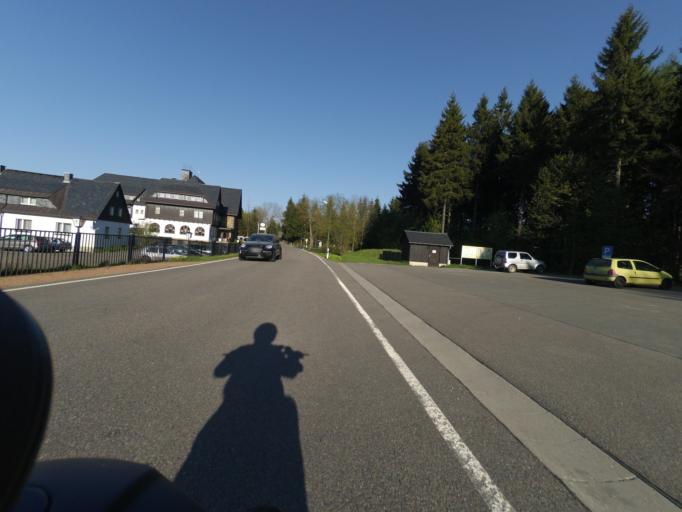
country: DE
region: Saxony
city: Altenberg
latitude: 50.7351
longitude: 13.6599
